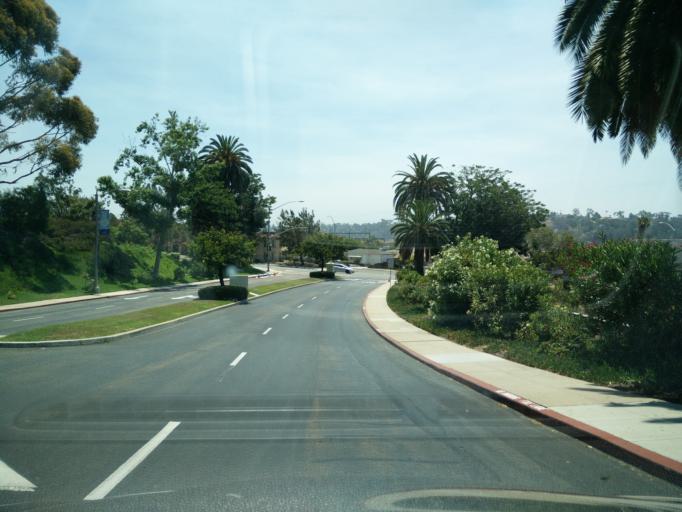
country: US
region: California
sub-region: San Diego County
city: San Diego
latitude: 32.7686
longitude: -117.1952
